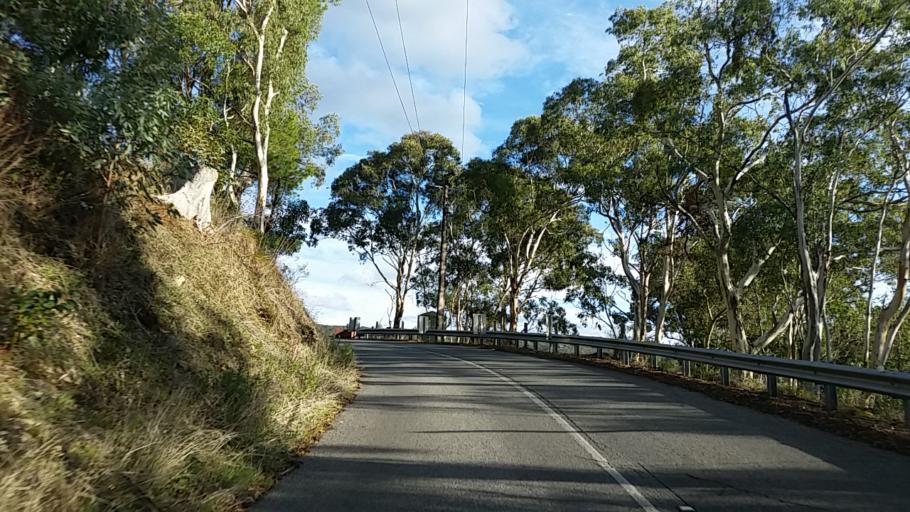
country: AU
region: South Australia
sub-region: Adelaide Hills
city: Adelaide Hills
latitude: -34.8892
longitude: 138.7490
